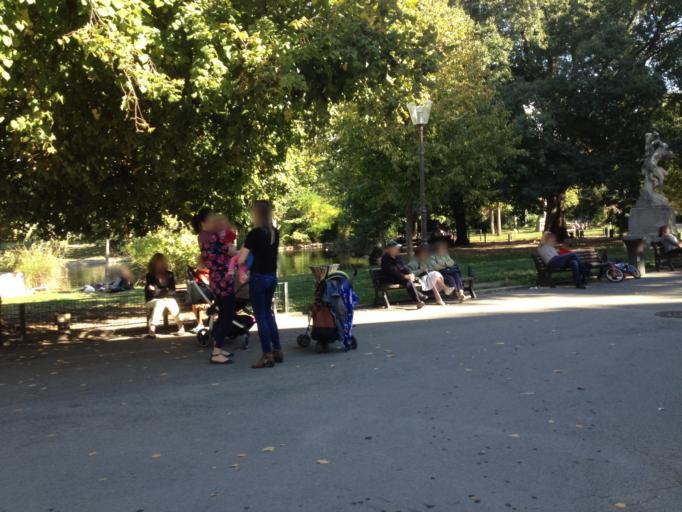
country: FR
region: Languedoc-Roussillon
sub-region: Departement de l'Herault
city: Montpellier
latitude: 43.6109
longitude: 3.8818
